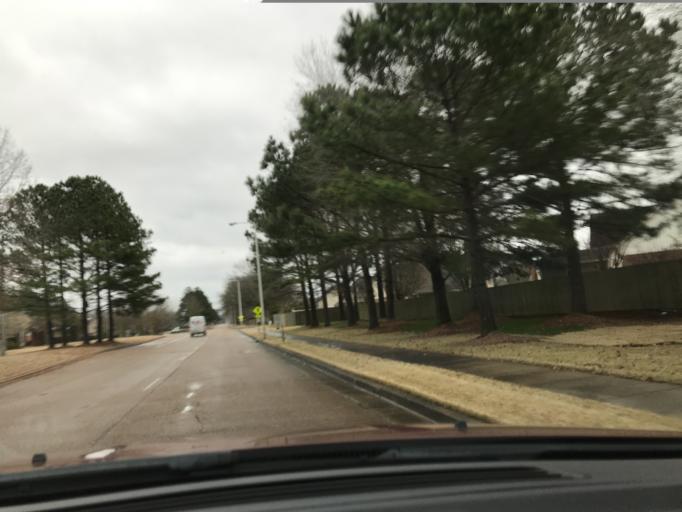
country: US
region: Tennessee
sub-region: Shelby County
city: Collierville
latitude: 35.0853
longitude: -89.6938
